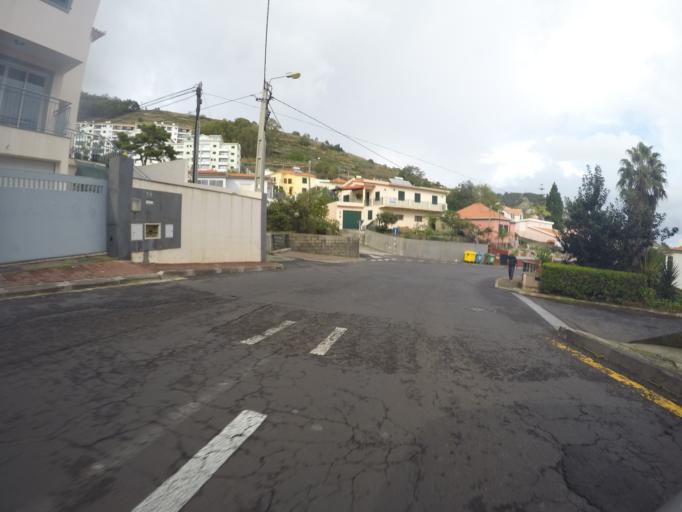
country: PT
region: Madeira
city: Canico
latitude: 32.6526
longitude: -16.8478
